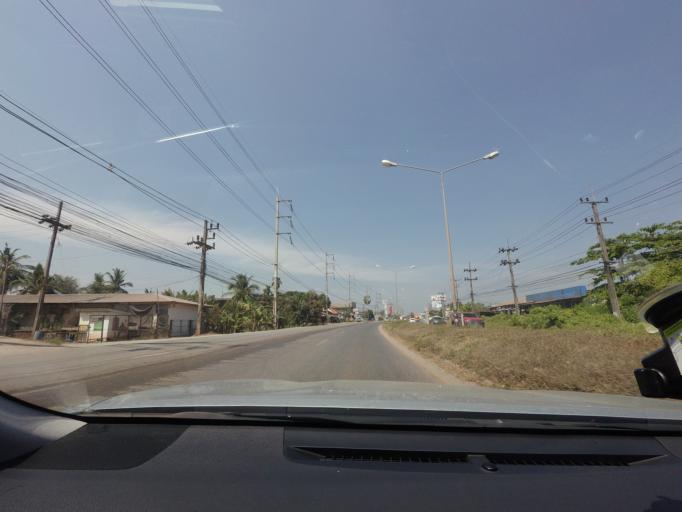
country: TH
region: Surat Thani
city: Surat Thani
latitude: 9.1468
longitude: 99.4028
